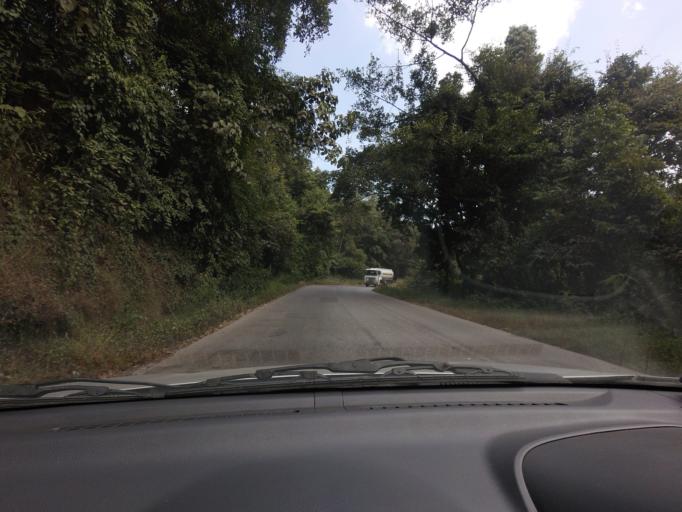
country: IN
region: Karnataka
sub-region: Hassan
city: Sakleshpur
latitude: 12.8334
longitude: 75.6487
